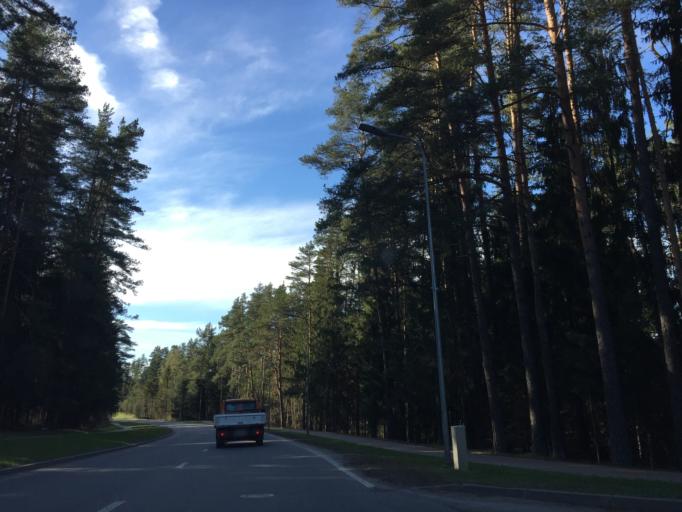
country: LV
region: Valkas Rajons
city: Valka
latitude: 57.7841
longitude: 26.0021
